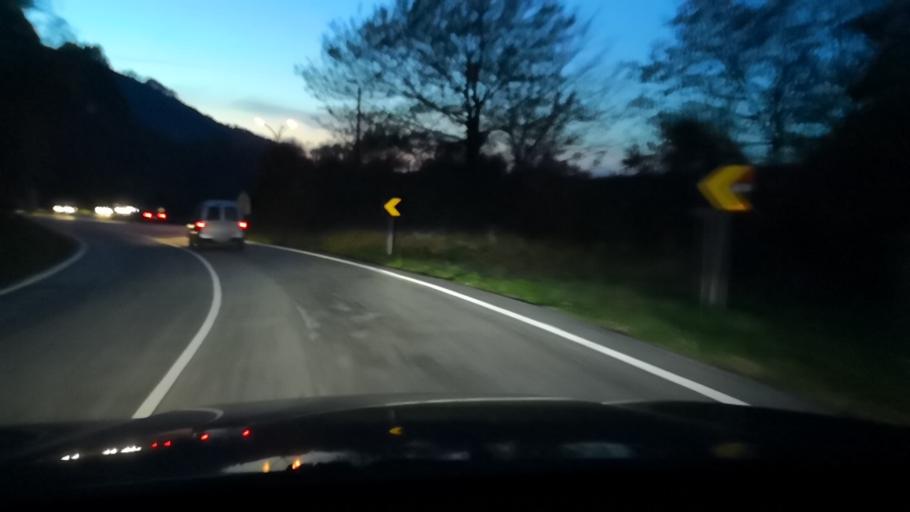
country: PT
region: Porto
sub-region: Baiao
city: Baiao
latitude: 41.2263
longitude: -7.9990
